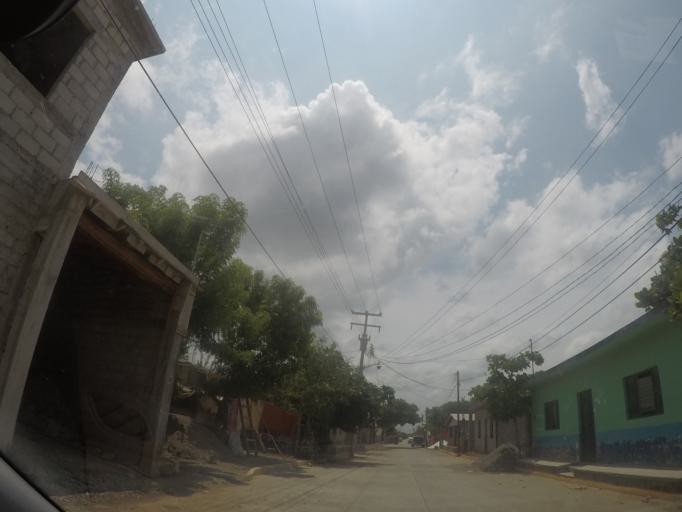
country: MX
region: Oaxaca
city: El Espinal
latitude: 16.5523
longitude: -94.9460
